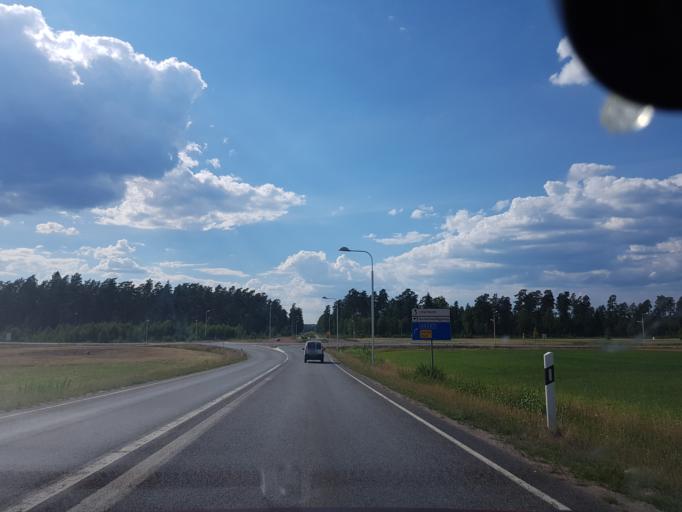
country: SE
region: Joenkoeping
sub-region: Gislaveds Kommun
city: Gislaved
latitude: 57.2933
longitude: 13.5794
